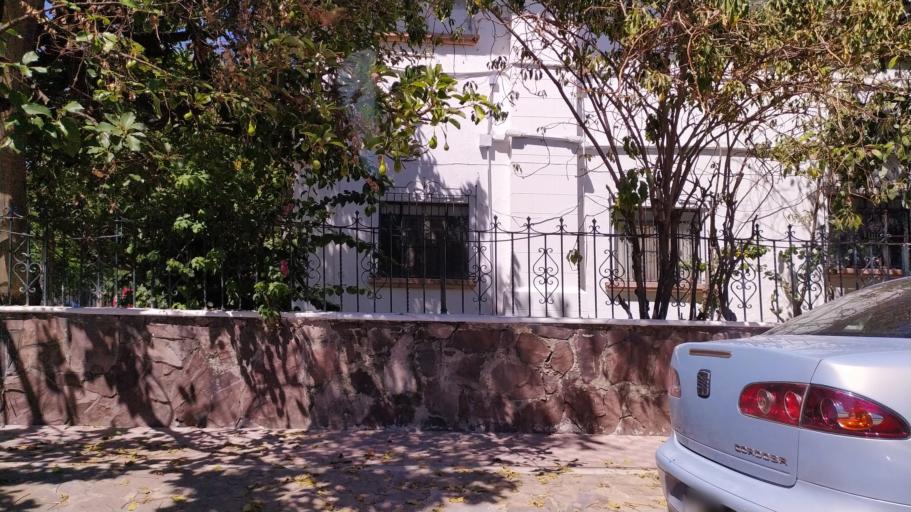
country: MX
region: Jalisco
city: Guadalajara
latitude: 20.6719
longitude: -103.3910
